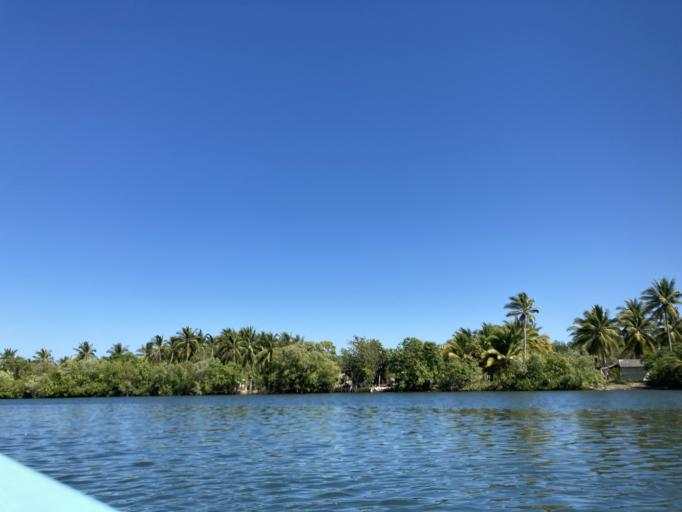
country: GT
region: Jutiapa
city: Pasaco
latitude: 13.8080
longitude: -90.2706
